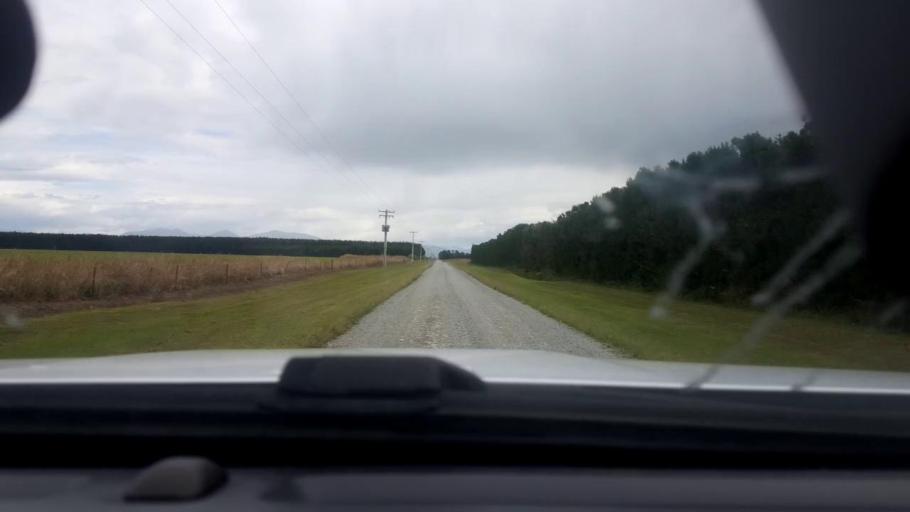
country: NZ
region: Canterbury
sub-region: Timaru District
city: Timaru
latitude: -44.1665
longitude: 171.4104
